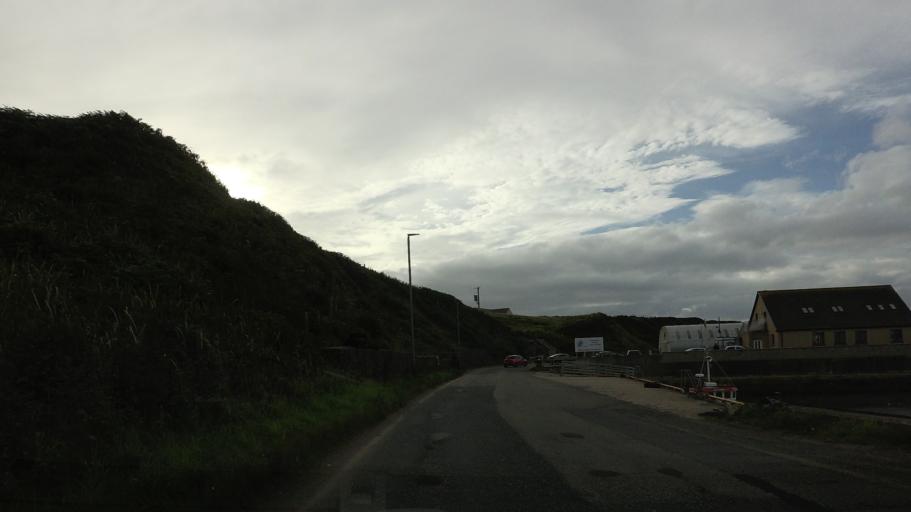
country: GB
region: Scotland
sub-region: Highland
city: Wick
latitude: 58.6378
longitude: -3.1610
